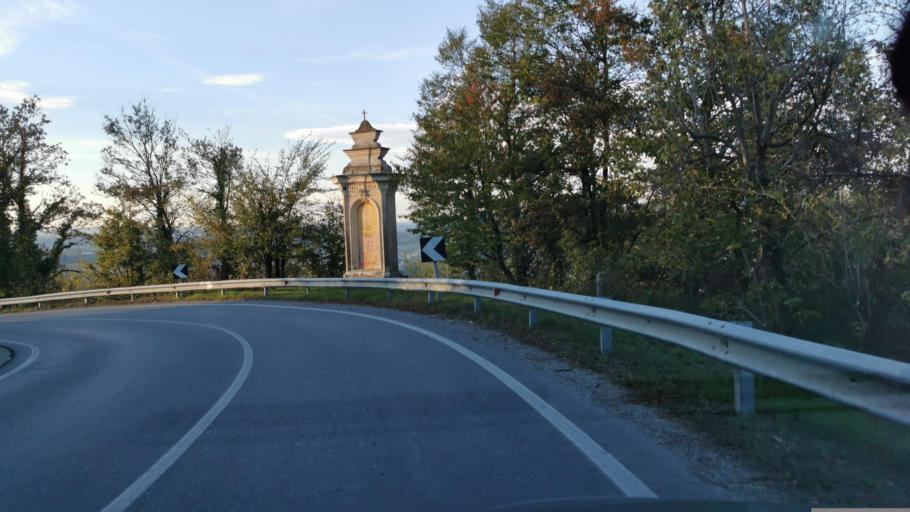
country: IT
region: Piedmont
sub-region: Provincia di Cuneo
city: Dogliani
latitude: 44.5212
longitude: 7.9514
